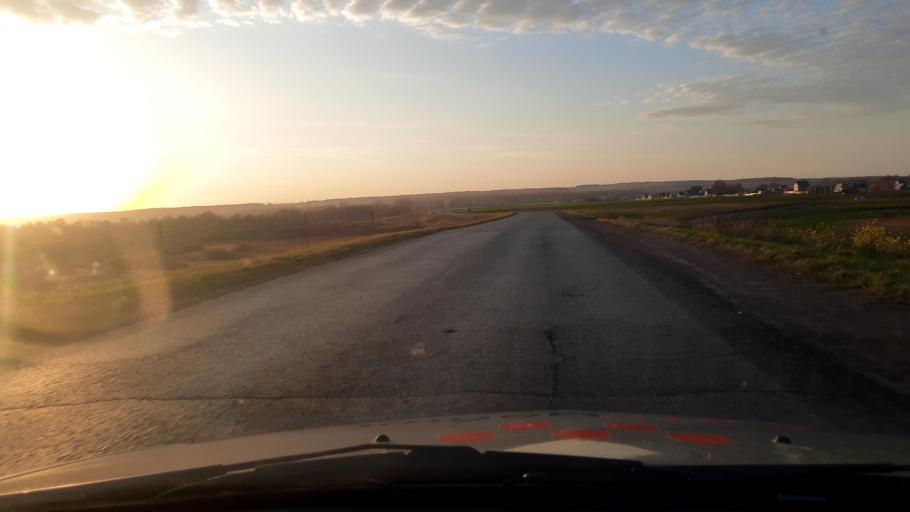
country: RU
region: Bashkortostan
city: Mikhaylovka
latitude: 54.8298
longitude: 55.9624
